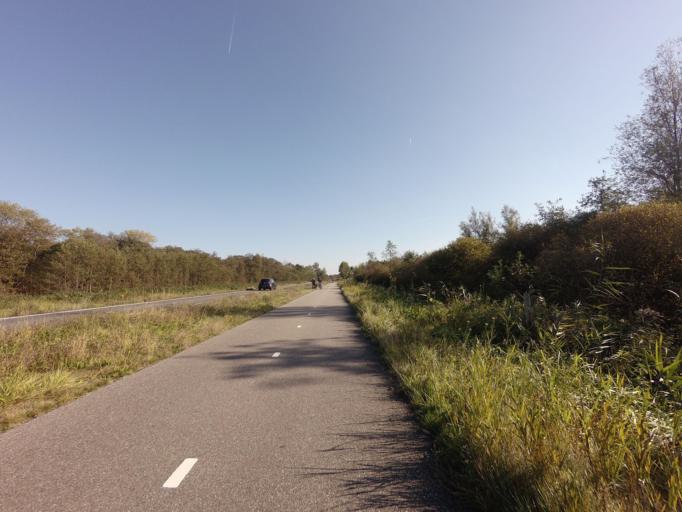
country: NL
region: North Holland
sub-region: Gemeente Wijdemeren
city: Kortenhoef
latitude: 52.2730
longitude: 5.1164
